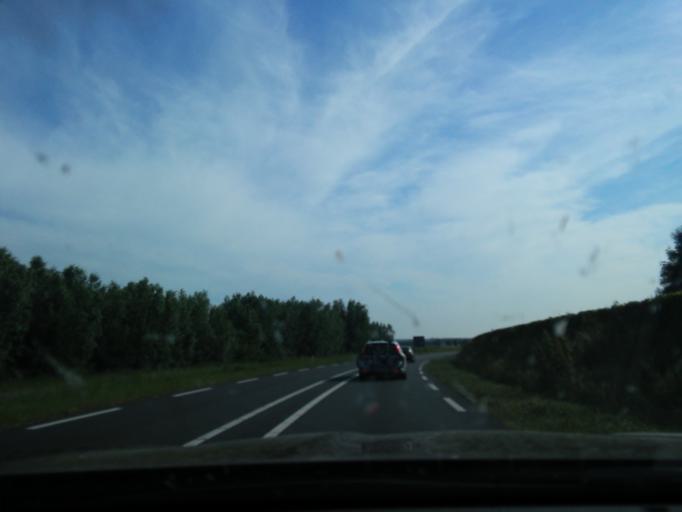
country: BE
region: Flanders
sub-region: Provincie Oost-Vlaanderen
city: Maldegem
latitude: 51.2704
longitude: 3.4642
